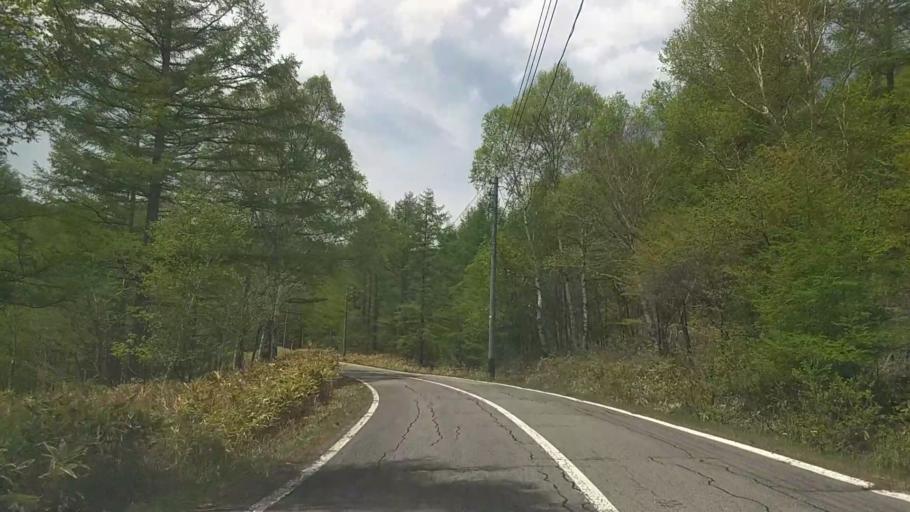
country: JP
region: Nagano
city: Saku
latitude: 36.0639
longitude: 138.3898
